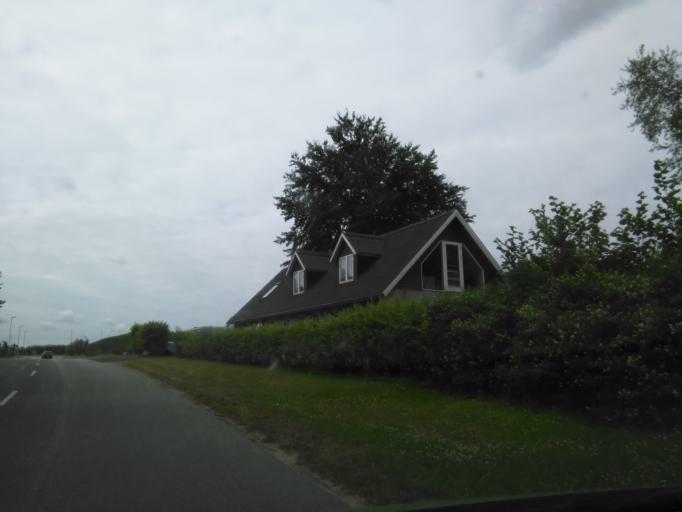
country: DK
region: Central Jutland
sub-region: Arhus Kommune
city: Marslet
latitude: 56.0630
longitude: 10.1566
